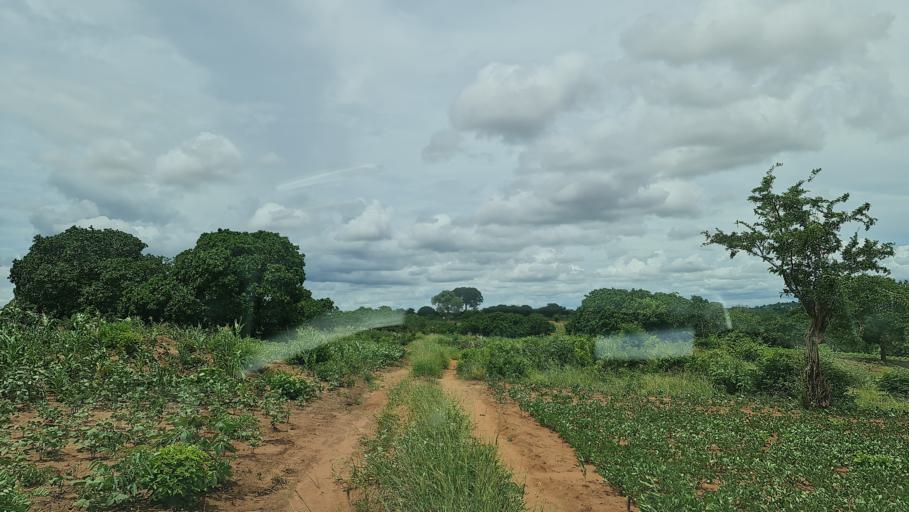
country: MZ
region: Nampula
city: Nacala
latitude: -14.7822
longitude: 39.9823
